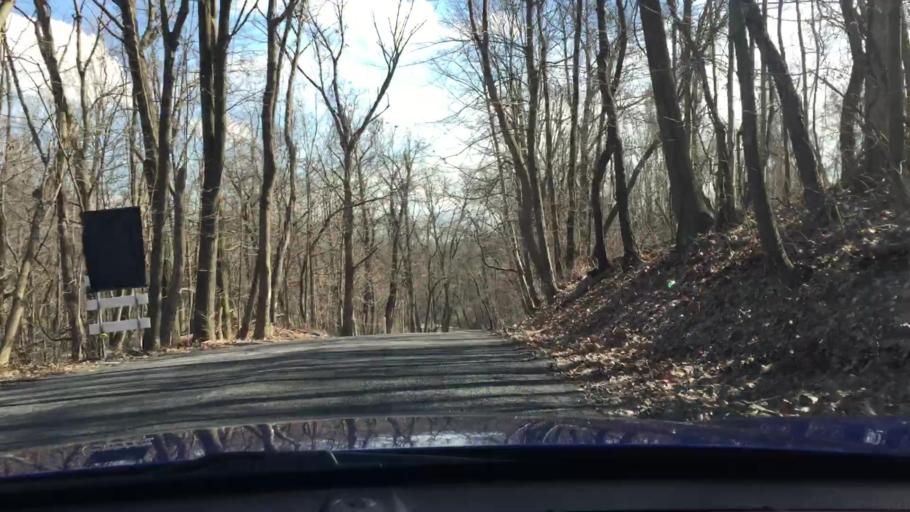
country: US
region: Pennsylvania
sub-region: Washington County
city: Thompsonville
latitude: 40.3102
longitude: -80.1439
